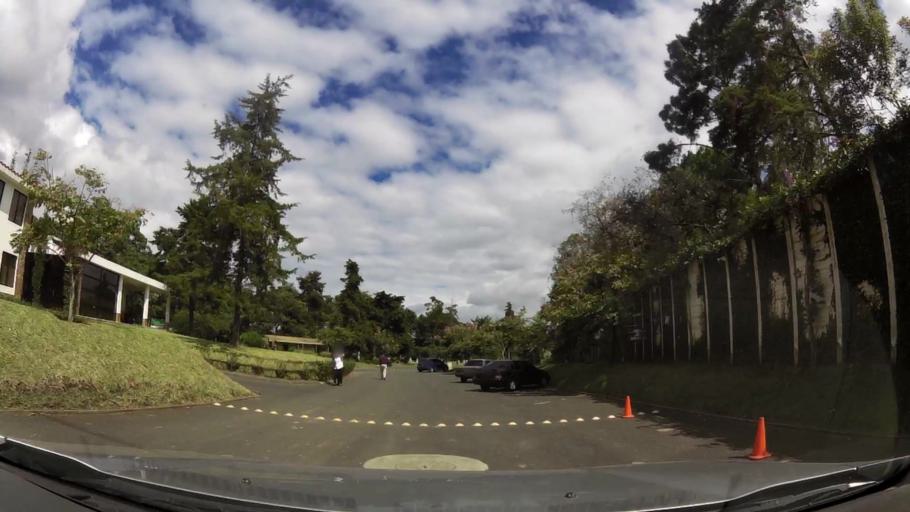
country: GT
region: Guatemala
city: Chinautla
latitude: 14.6873
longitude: -90.5433
